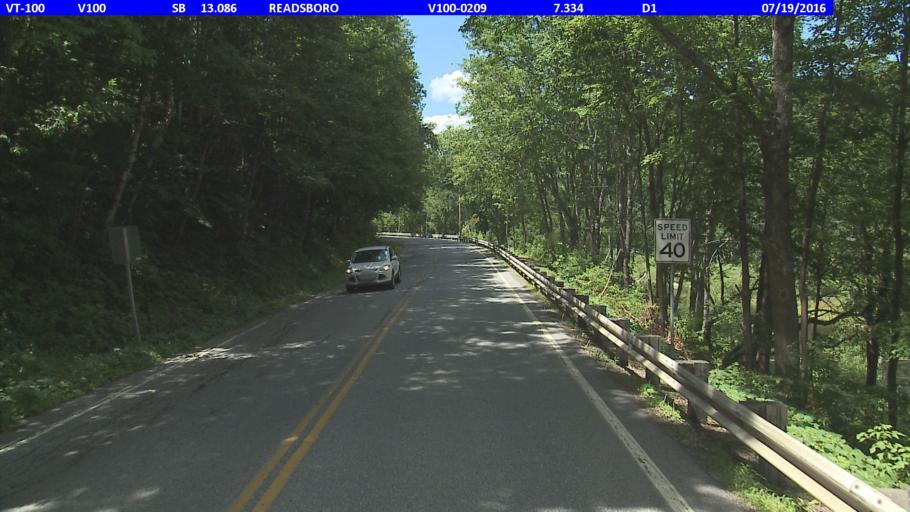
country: US
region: Massachusetts
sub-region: Franklin County
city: Charlemont
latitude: 42.7707
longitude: -72.9419
